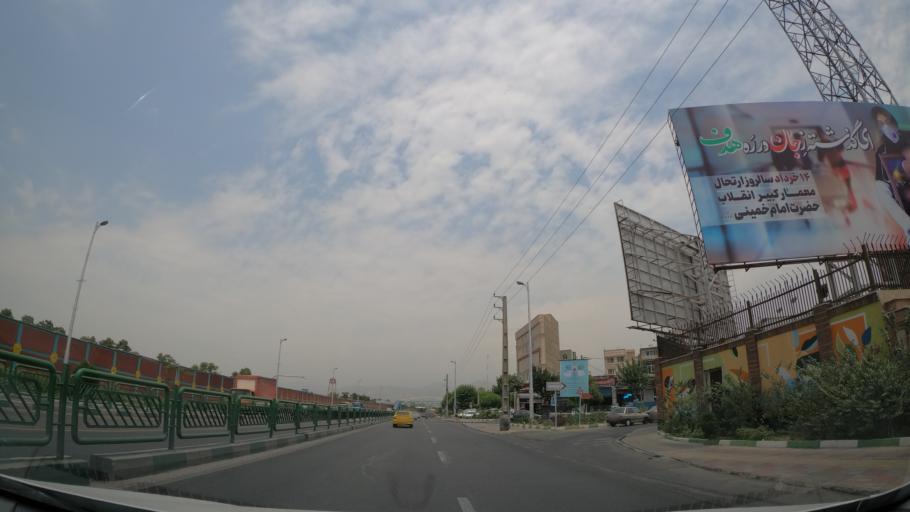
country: IR
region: Tehran
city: Tehran
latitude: 35.6869
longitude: 51.3413
